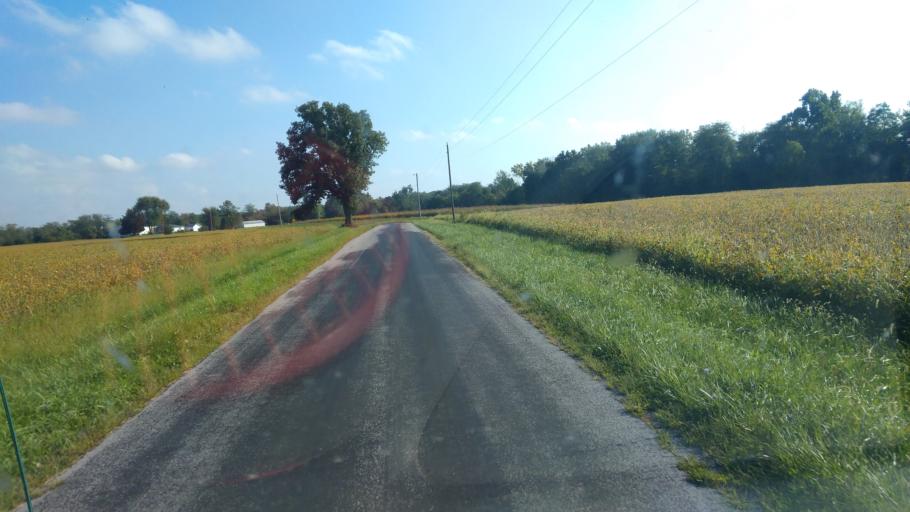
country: US
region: Ohio
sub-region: Hardin County
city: Forest
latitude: 40.7224
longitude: -83.4602
